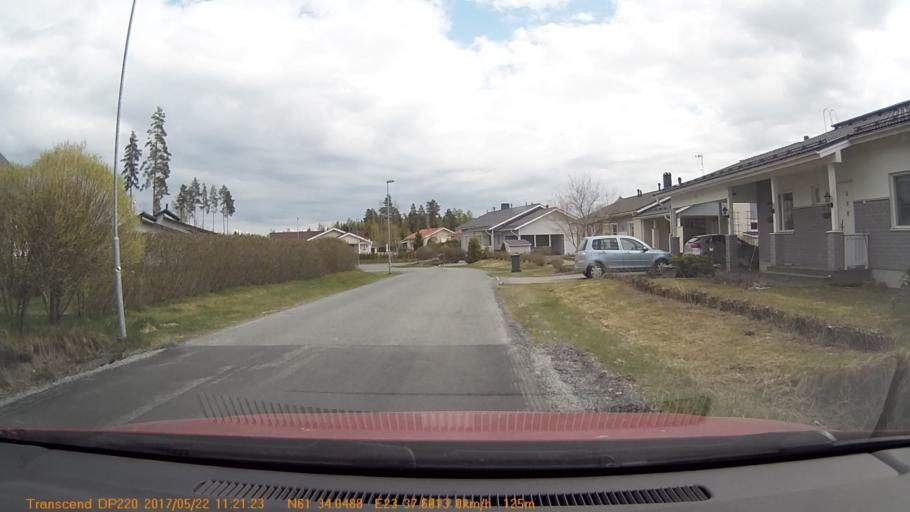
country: FI
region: Pirkanmaa
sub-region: Tampere
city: Yloejaervi
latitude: 61.5675
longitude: 23.6267
